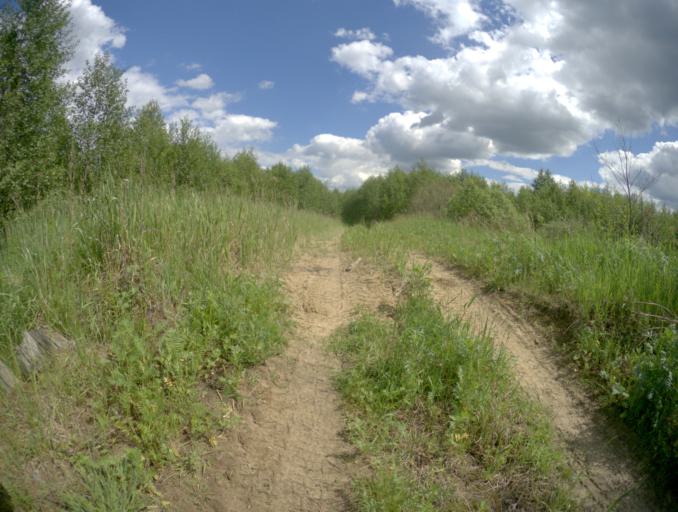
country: RU
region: Vladimir
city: Velikodvorskiy
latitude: 55.2719
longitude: 40.8522
